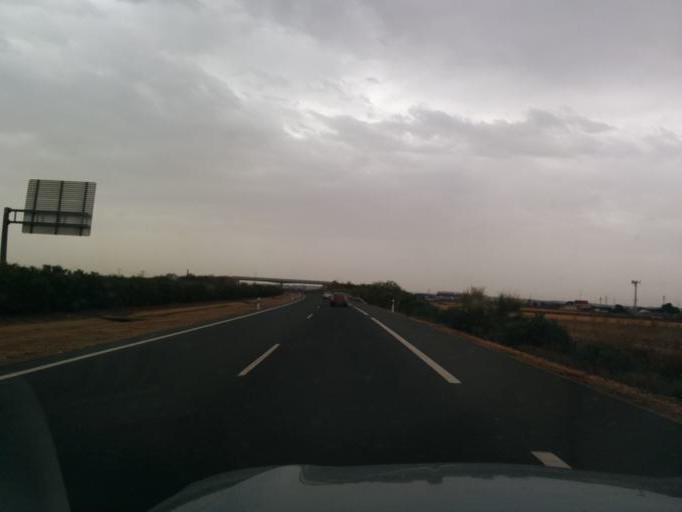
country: ES
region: Andalusia
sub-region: Provincia de Huelva
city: San Juan del Puerto
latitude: 37.3167
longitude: -6.9004
